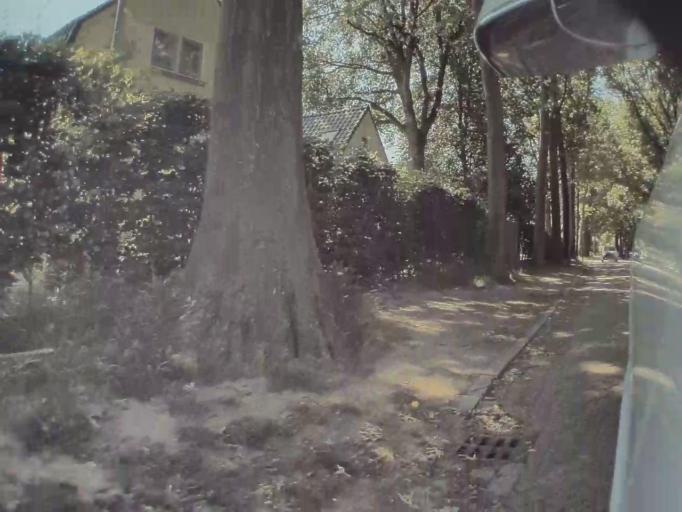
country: NL
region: North Brabant
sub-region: Gemeente 's-Hertogenbosch
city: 's-Hertogenbosch
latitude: 51.7085
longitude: 5.3672
